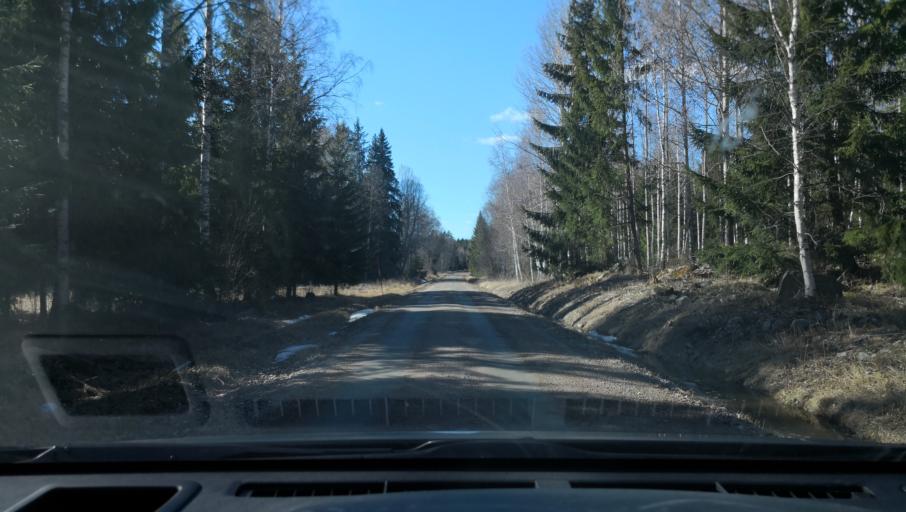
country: SE
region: Vaestmanland
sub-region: Sala Kommun
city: Sala
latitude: 60.1150
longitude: 16.6772
